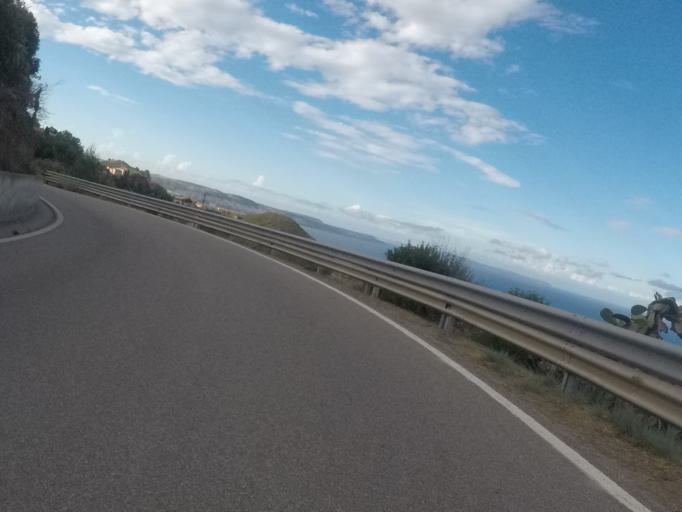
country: IT
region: Sardinia
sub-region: Provincia di Carbonia-Iglesias
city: Gonnesa
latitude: 39.3229
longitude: 8.4358
